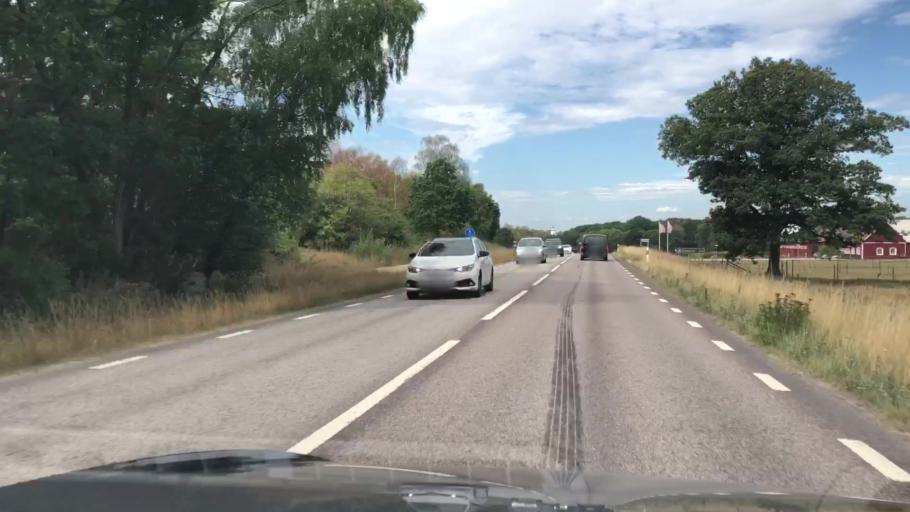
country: SE
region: Blekinge
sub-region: Karlskrona Kommun
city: Jaemjoe
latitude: 56.1872
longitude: 15.7138
